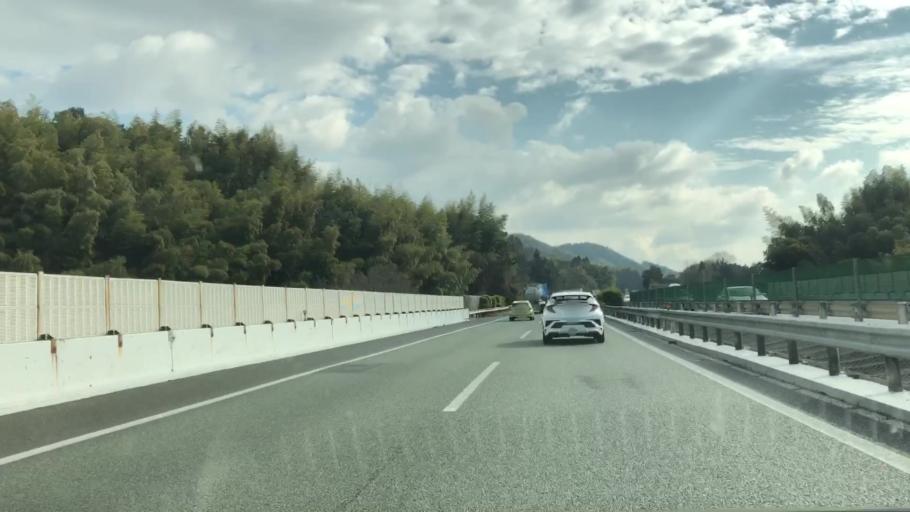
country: JP
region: Fukuoka
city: Setakamachi-takayanagi
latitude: 33.1122
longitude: 130.5310
